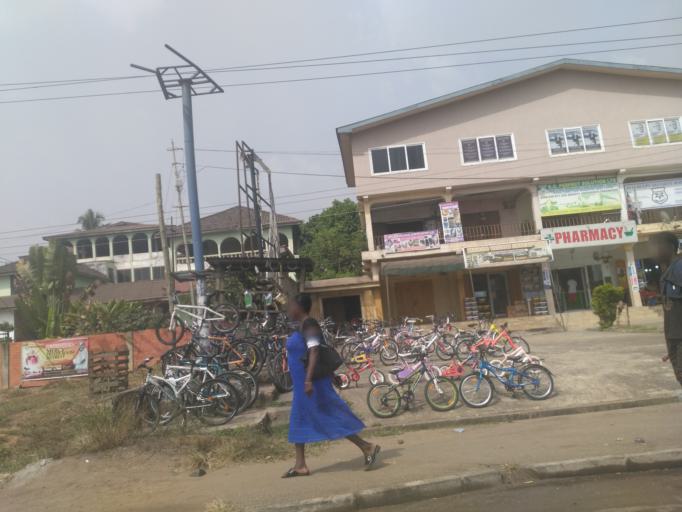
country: GH
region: Ashanti
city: Kumasi
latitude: 6.6877
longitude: -1.5838
